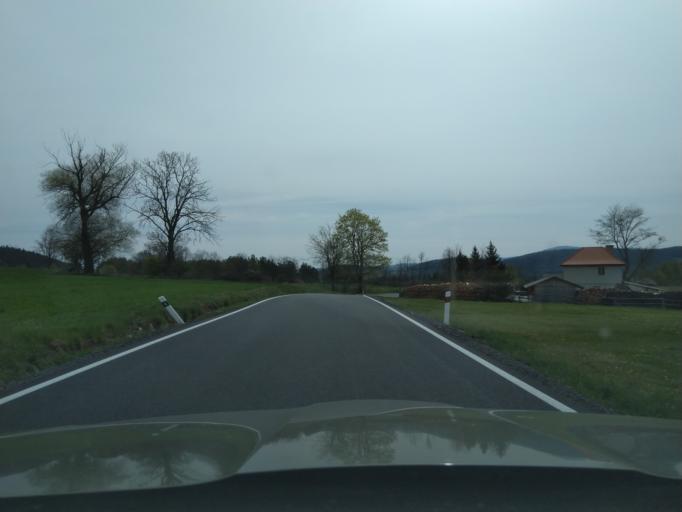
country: CZ
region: Jihocesky
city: Vacov
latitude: 49.1213
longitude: 13.7456
